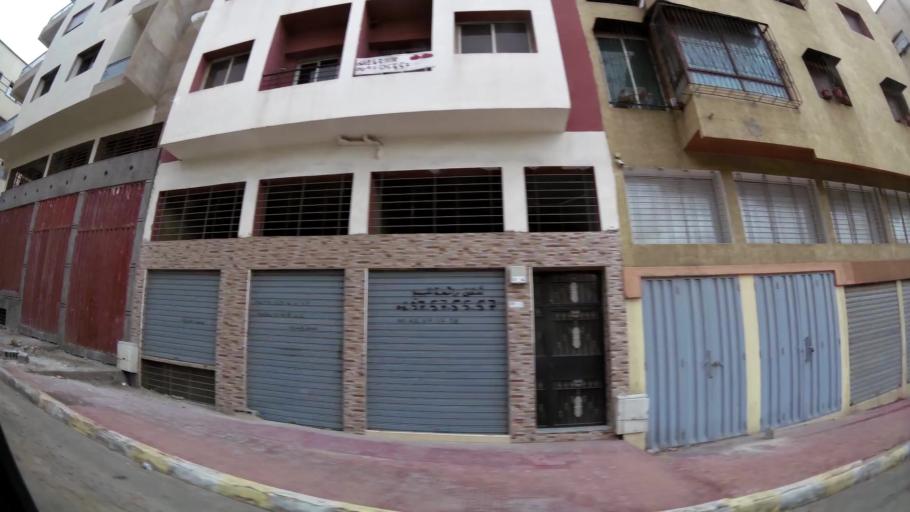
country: MA
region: Grand Casablanca
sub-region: Mediouna
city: Tit Mellil
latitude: 33.5608
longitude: -7.5311
